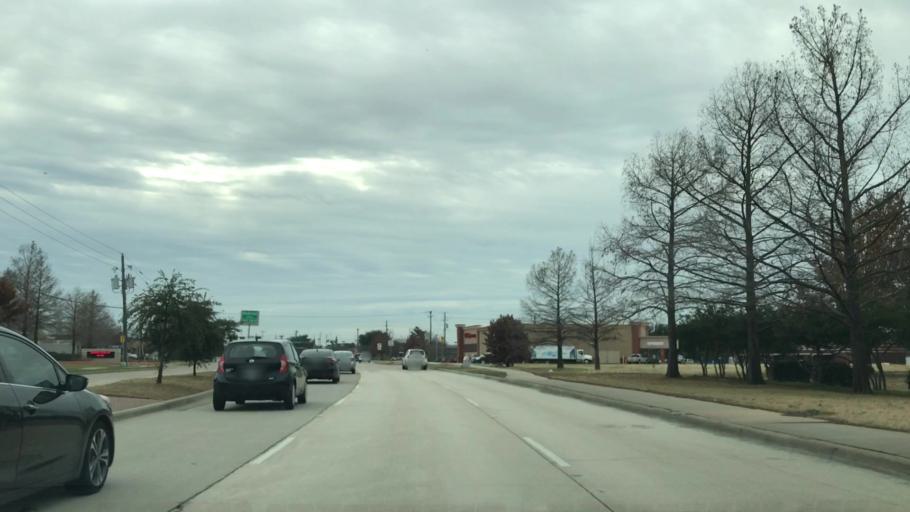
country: US
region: Texas
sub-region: Denton County
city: The Colony
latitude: 33.0270
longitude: -96.8849
